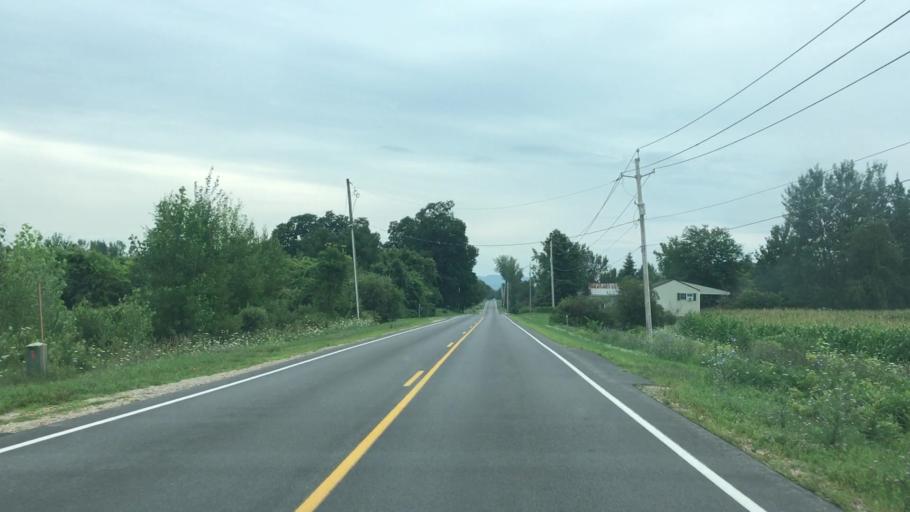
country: US
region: New York
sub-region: Clinton County
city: Peru
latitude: 44.5944
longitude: -73.5728
